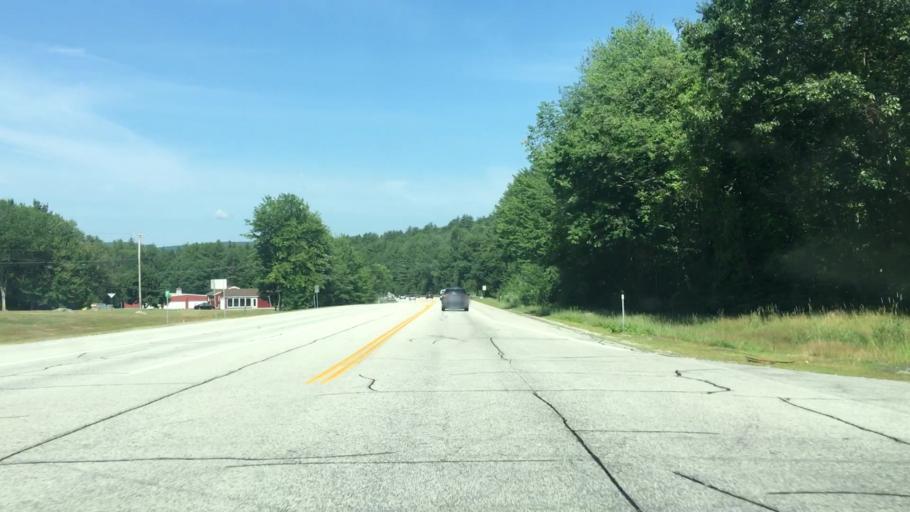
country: US
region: New Hampshire
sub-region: Merrimack County
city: Henniker
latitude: 43.1847
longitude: -71.7884
